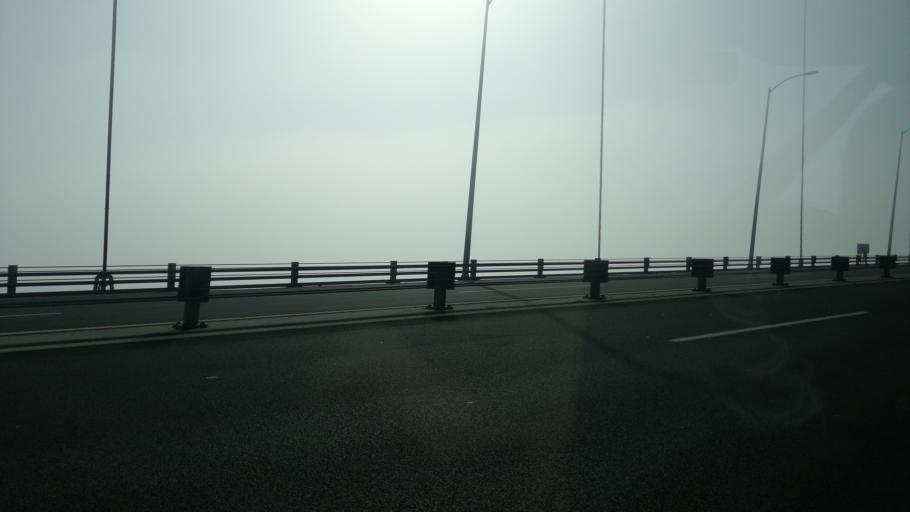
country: TR
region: Kocaeli
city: Tavsancil
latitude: 40.7598
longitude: 29.5166
